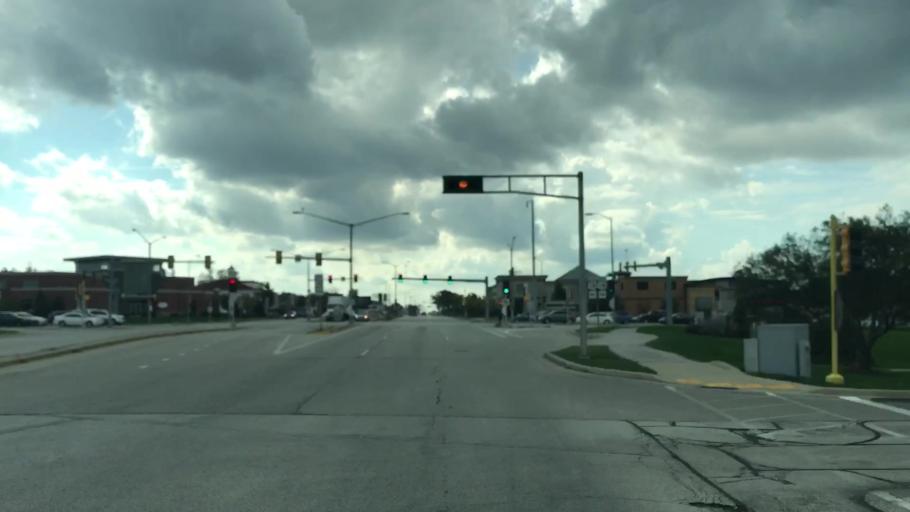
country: US
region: Wisconsin
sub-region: Waukesha County
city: Brookfield
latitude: 43.0370
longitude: -88.1068
